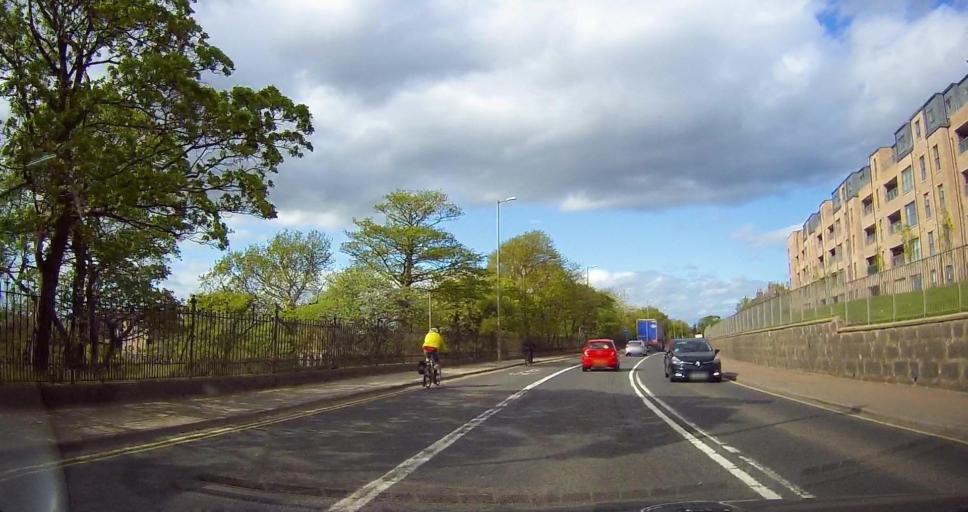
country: GB
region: Scotland
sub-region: Aberdeen City
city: Aberdeen
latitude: 57.1324
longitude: -2.0948
